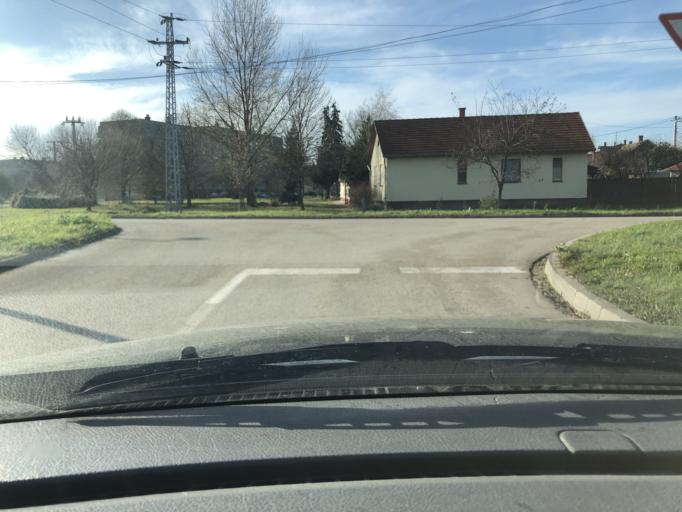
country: HU
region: Csongrad
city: Csongrad
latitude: 46.7099
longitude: 20.1661
